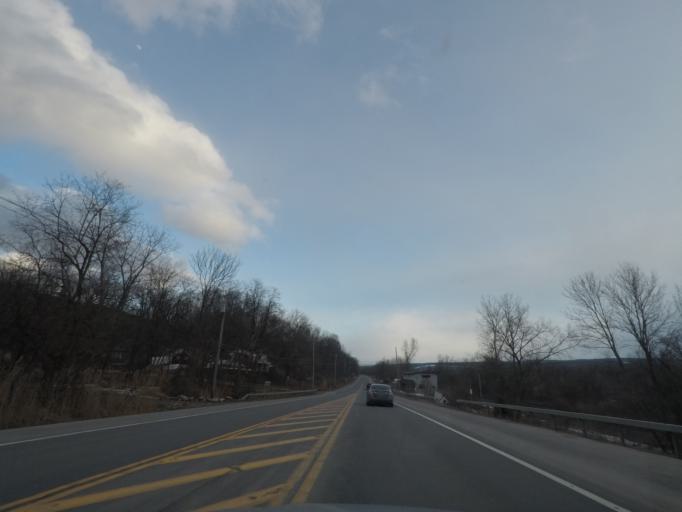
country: US
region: New York
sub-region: Herkimer County
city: Frankfort
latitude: 43.0430
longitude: -75.0599
